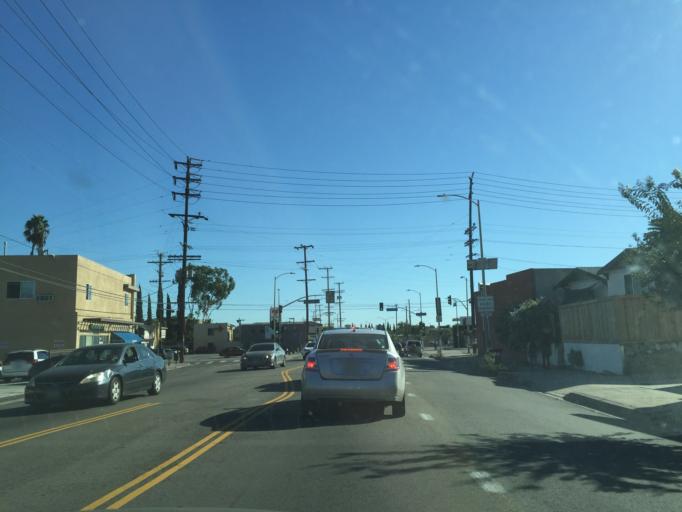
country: US
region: California
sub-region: Los Angeles County
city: Silver Lake
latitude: 34.0916
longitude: -118.2866
